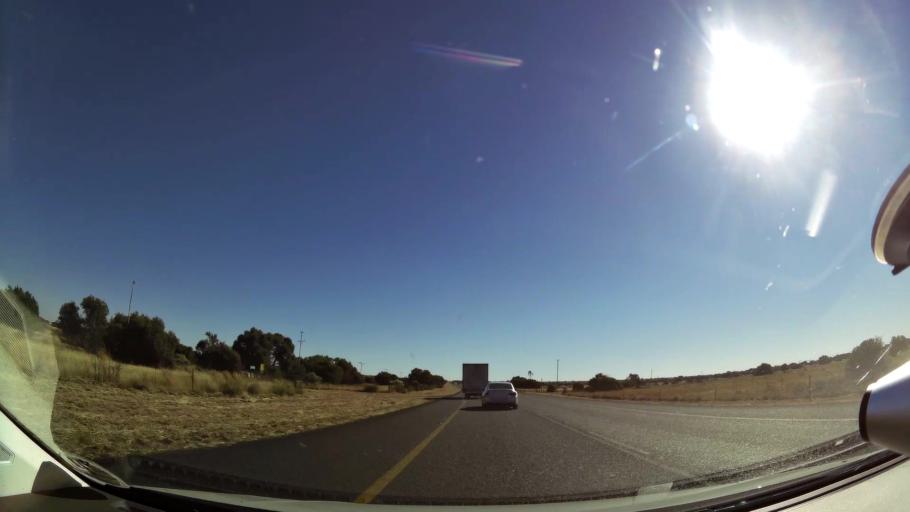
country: ZA
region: Northern Cape
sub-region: Frances Baard District Municipality
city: Warrenton
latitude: -28.2238
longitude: 24.8495
